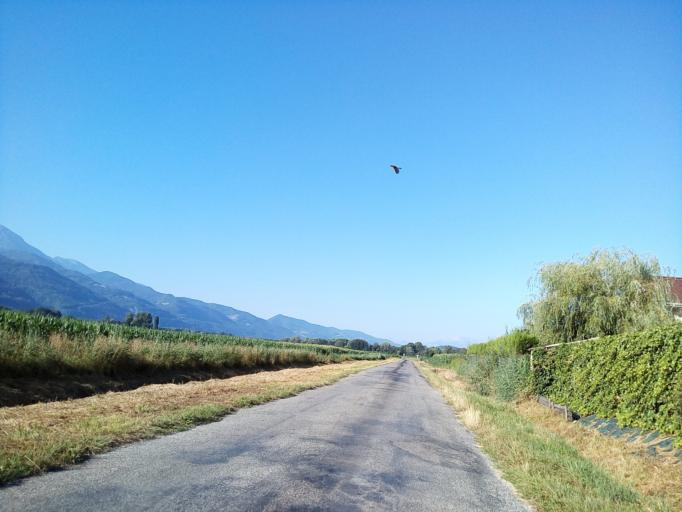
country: FR
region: Rhone-Alpes
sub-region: Departement de l'Isere
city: Lumbin
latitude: 45.3022
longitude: 5.9132
